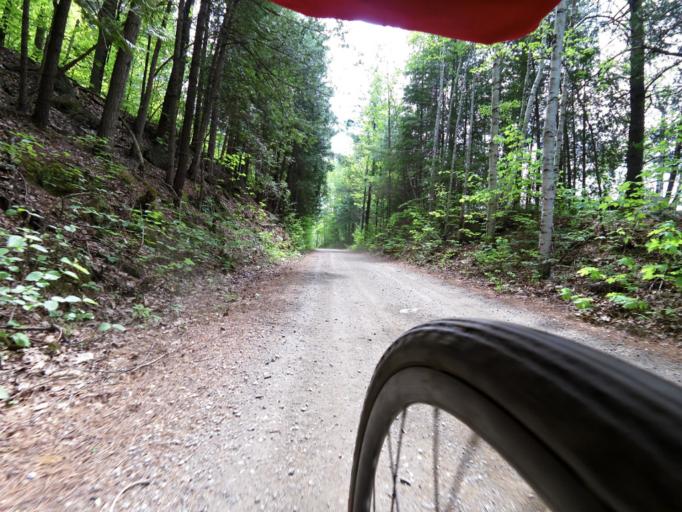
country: CA
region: Ontario
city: Renfrew
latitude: 45.1939
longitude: -76.6858
